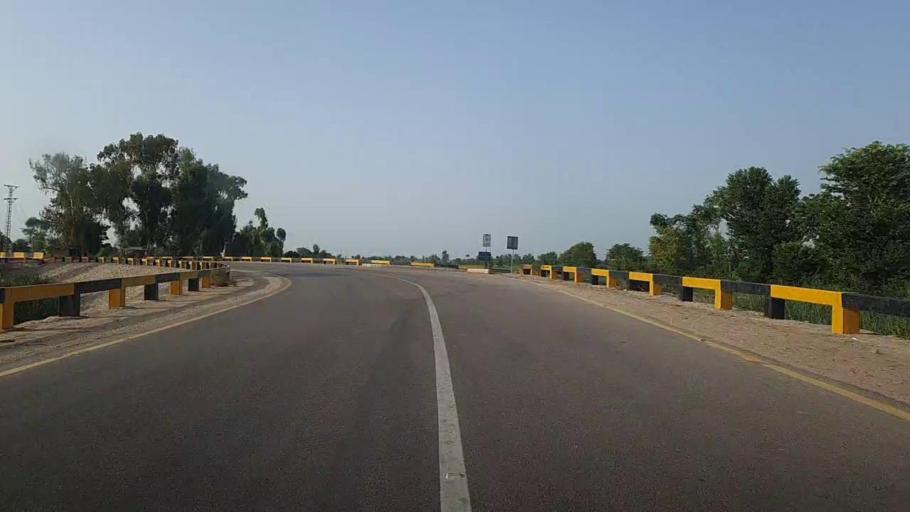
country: PK
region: Sindh
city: Naushahro Firoz
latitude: 26.7923
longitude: 68.1448
